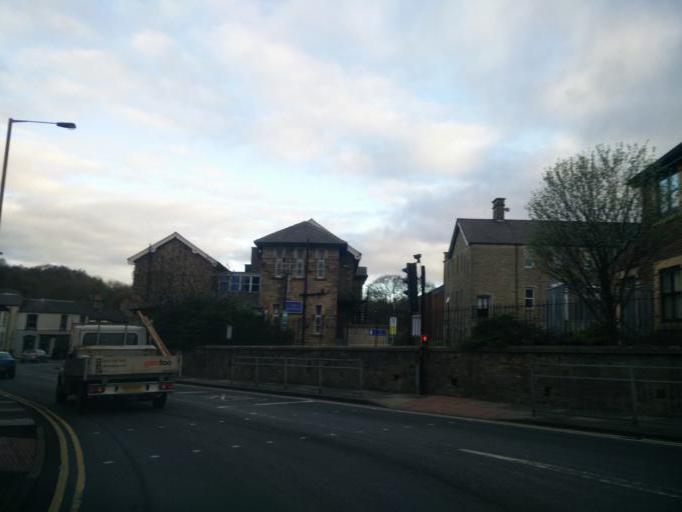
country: GB
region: England
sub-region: County Durham
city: Durham
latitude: 54.7750
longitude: -1.5843
